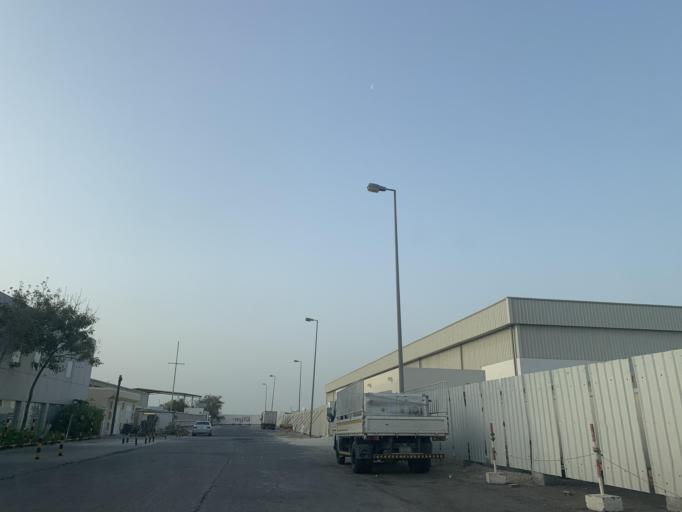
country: BH
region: Manama
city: Manama
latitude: 26.1967
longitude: 50.5939
